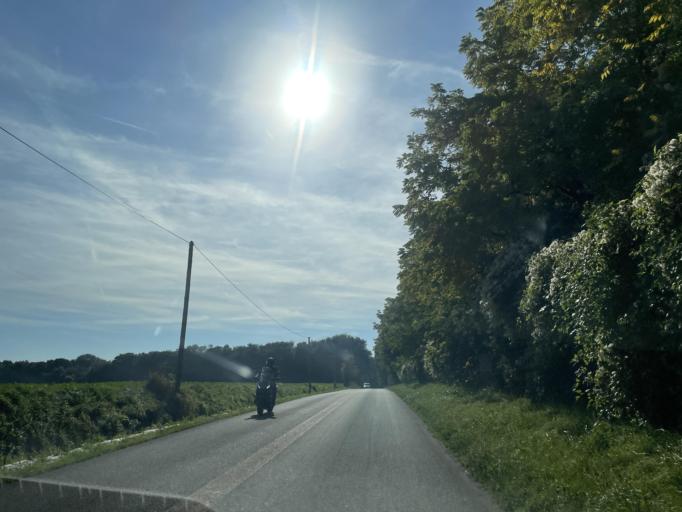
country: FR
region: Ile-de-France
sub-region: Departement de Seine-et-Marne
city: Saint-Jean-les-Deux-Jumeaux
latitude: 48.9393
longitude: 2.9859
